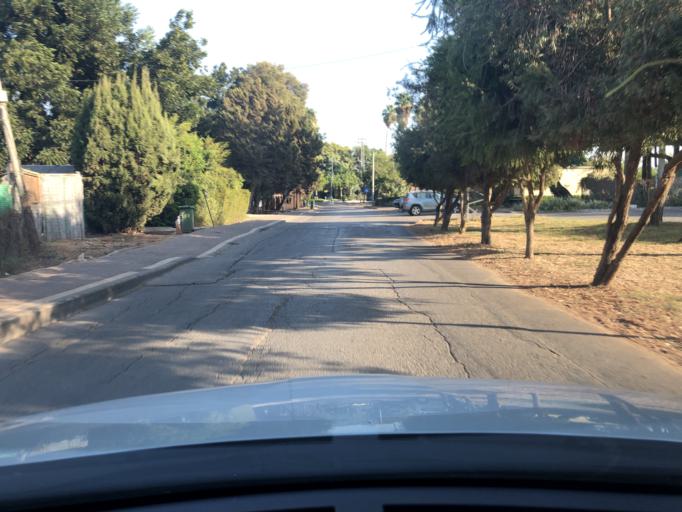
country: IL
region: Central District
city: Hod HaSharon
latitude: 32.1400
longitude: 34.9069
